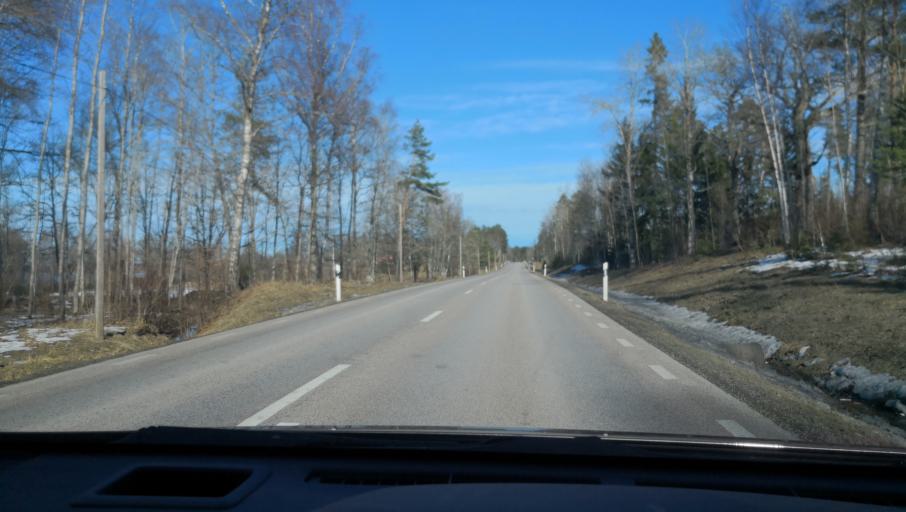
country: SE
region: Uppsala
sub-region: Osthammars Kommun
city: Osterbybruk
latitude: 60.1627
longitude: 17.8405
